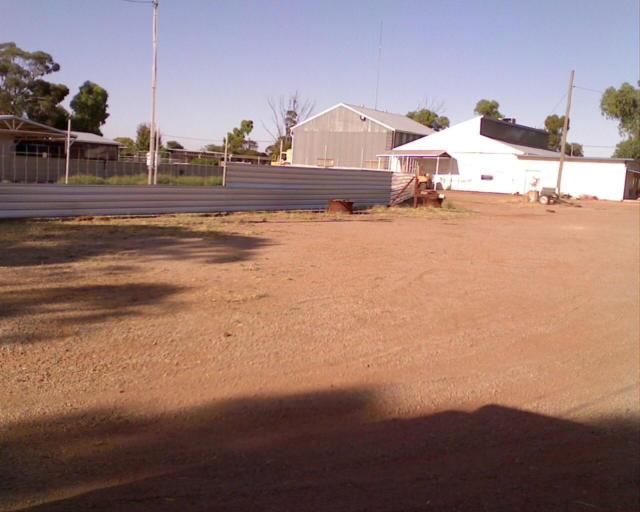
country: AU
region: Western Australia
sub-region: Merredin
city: Merredin
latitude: -31.1146
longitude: 117.7888
